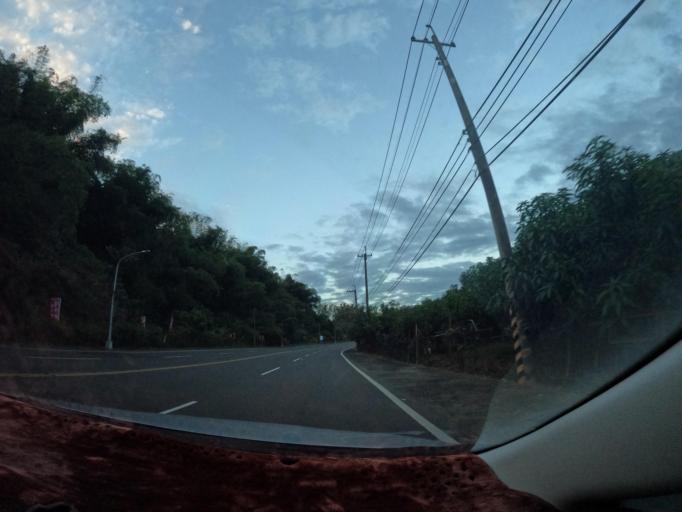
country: TW
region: Taiwan
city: Yujing
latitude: 23.0671
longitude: 120.4220
